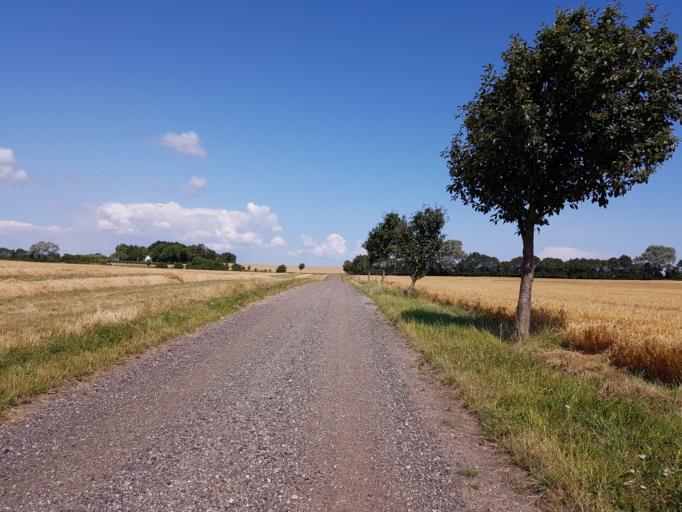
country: DK
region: Zealand
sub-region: Guldborgsund Kommune
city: Nykobing Falster
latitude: 54.5707
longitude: 11.9524
